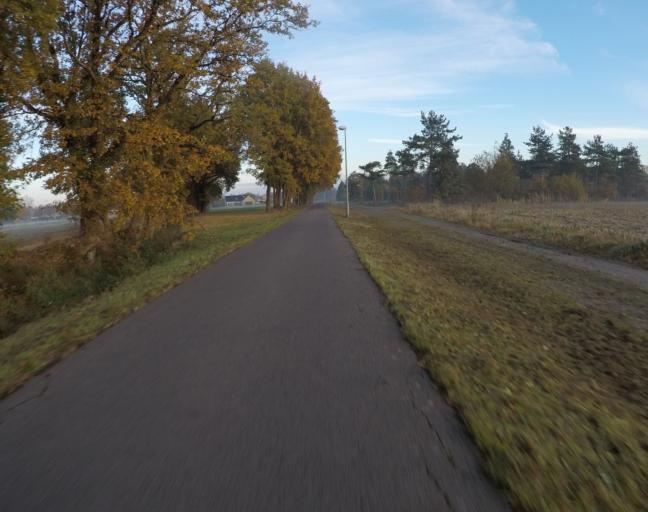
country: BE
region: Flanders
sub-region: Provincie Vlaams-Brabant
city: Begijnendijk
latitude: 51.0413
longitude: 4.8249
